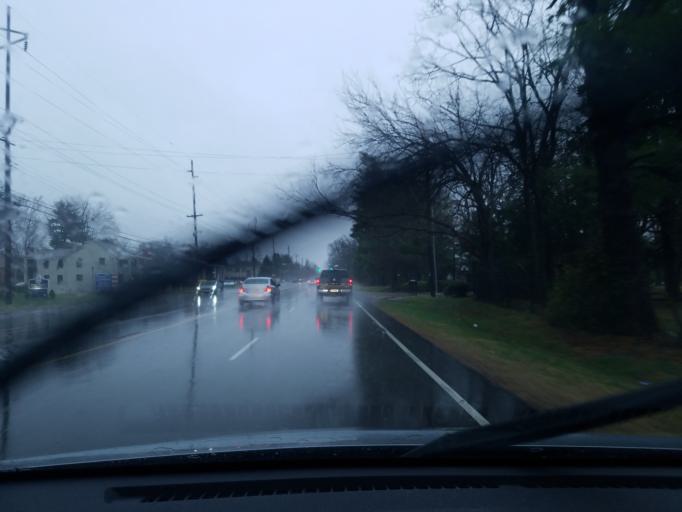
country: US
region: Kentucky
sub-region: Jefferson County
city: Lyndon
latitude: 38.2483
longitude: -85.6010
